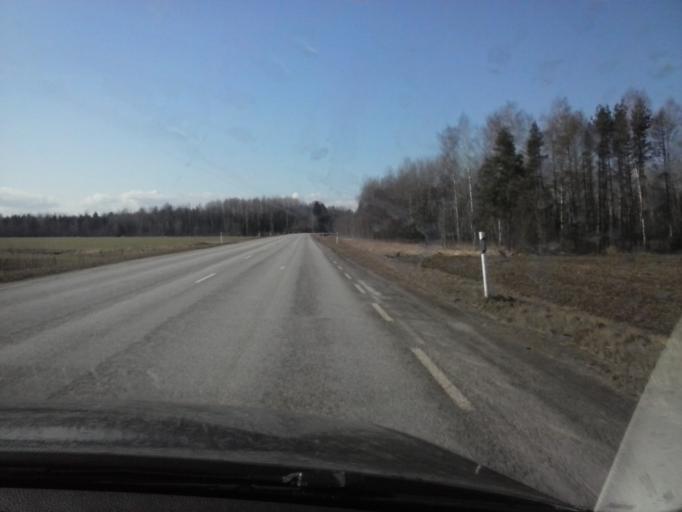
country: EE
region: Tartu
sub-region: Puhja vald
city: Puhja
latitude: 58.3274
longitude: 26.2697
